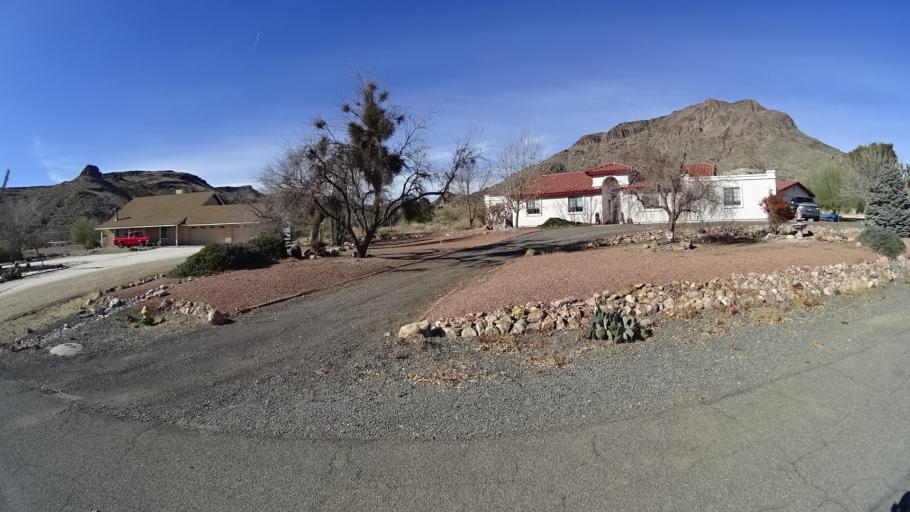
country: US
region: Arizona
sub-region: Mohave County
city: New Kingman-Butler
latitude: 35.2705
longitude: -114.0506
